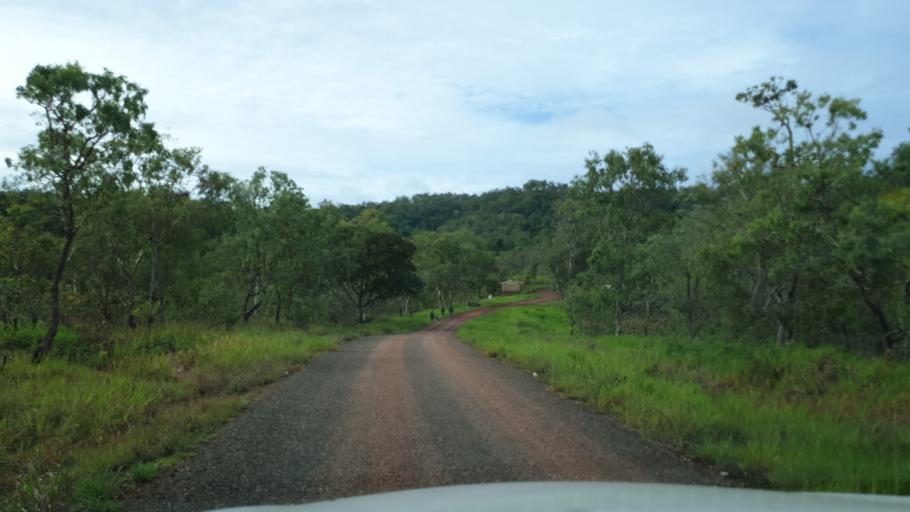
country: PG
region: National Capital
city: Port Moresby
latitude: -9.4340
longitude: 147.3967
